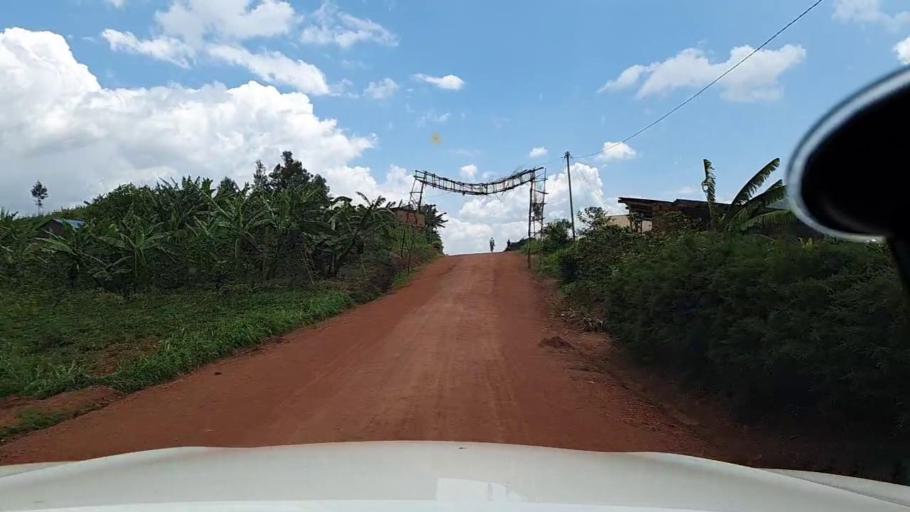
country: RW
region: Kigali
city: Kigali
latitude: -1.7699
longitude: 29.8419
